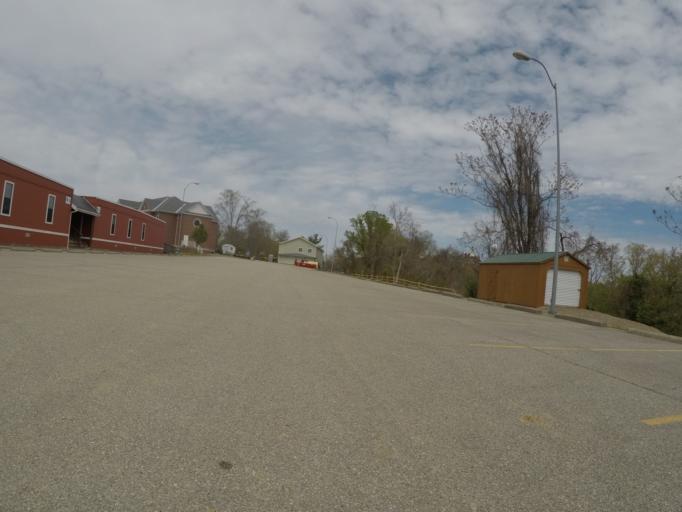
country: US
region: Ohio
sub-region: Lawrence County
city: Burlington
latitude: 38.3749
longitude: -82.5212
